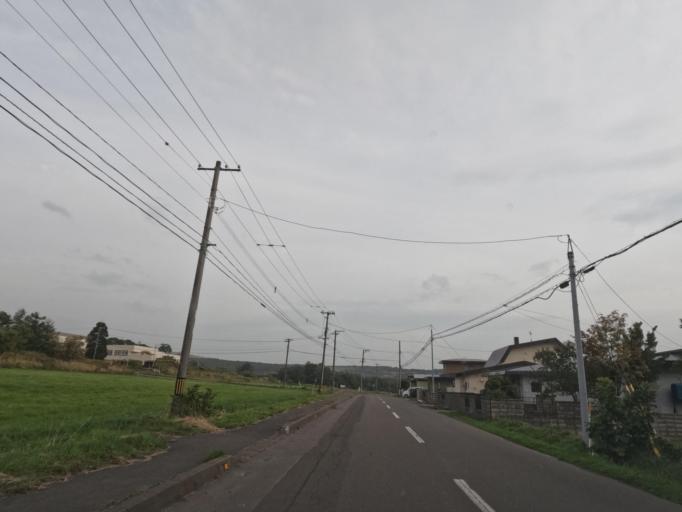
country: JP
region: Hokkaido
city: Date
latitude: 42.4211
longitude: 140.9109
